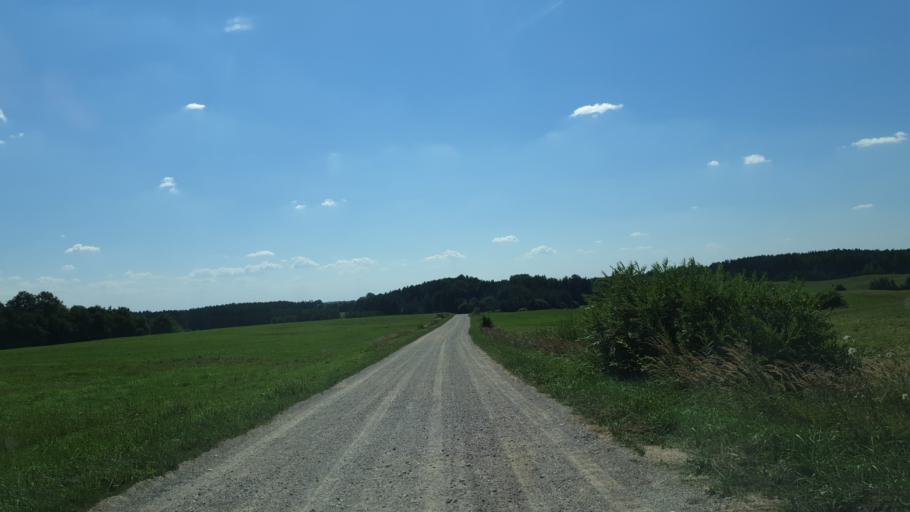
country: LT
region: Vilnius County
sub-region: Vilniaus Rajonas
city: Vievis
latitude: 54.8959
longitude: 24.8656
